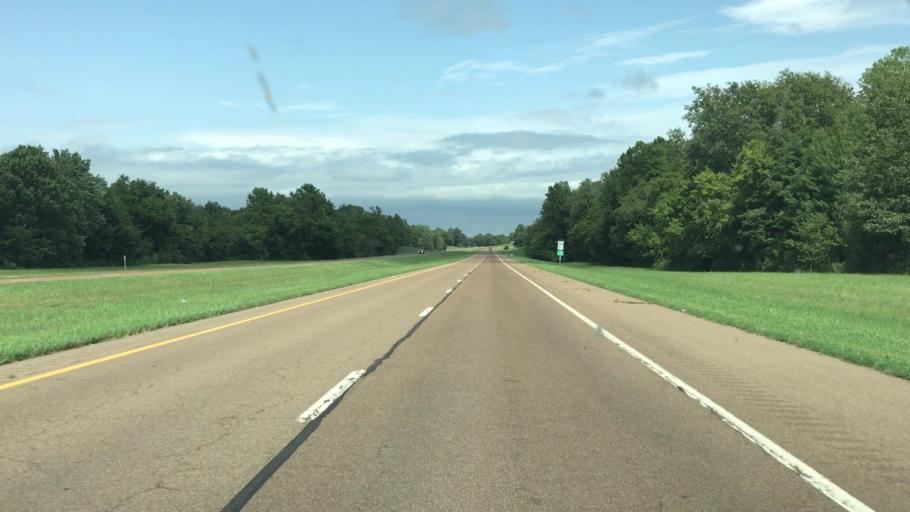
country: US
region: Tennessee
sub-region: Obion County
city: South Fulton
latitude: 36.4697
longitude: -88.9690
